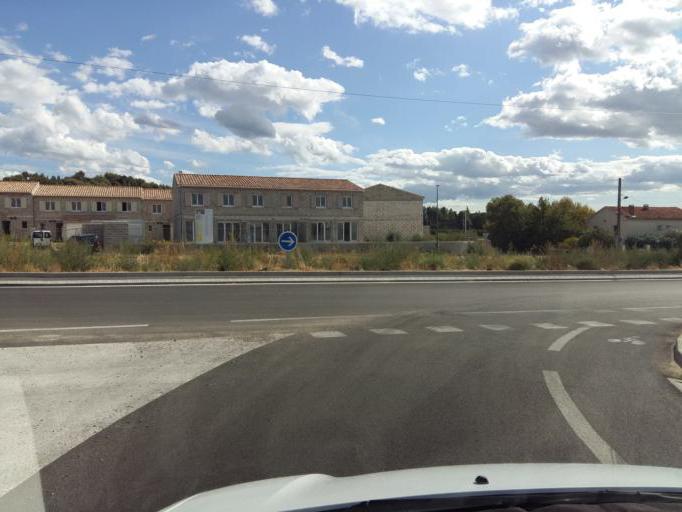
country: FR
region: Provence-Alpes-Cote d'Azur
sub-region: Departement du Vaucluse
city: Carpentras
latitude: 44.0593
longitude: 5.0703
